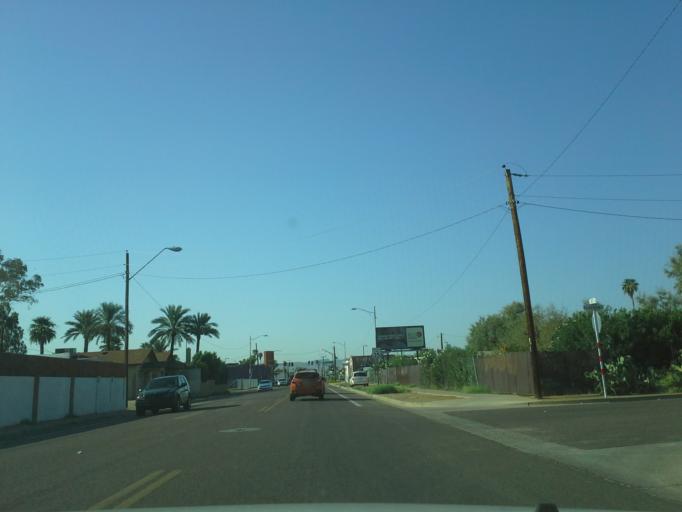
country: US
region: Arizona
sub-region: Maricopa County
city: Phoenix
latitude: 33.4607
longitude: -112.0913
